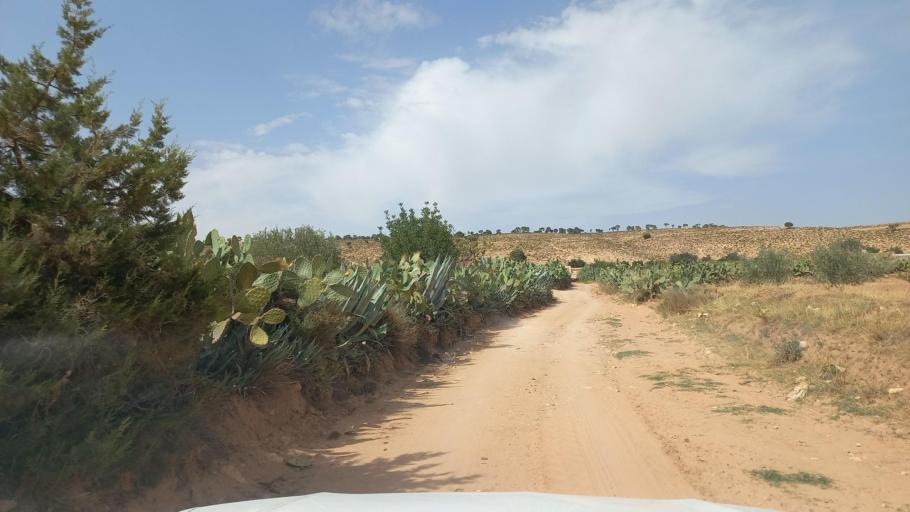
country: TN
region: Al Qasrayn
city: Kasserine
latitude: 35.3693
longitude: 8.8801
